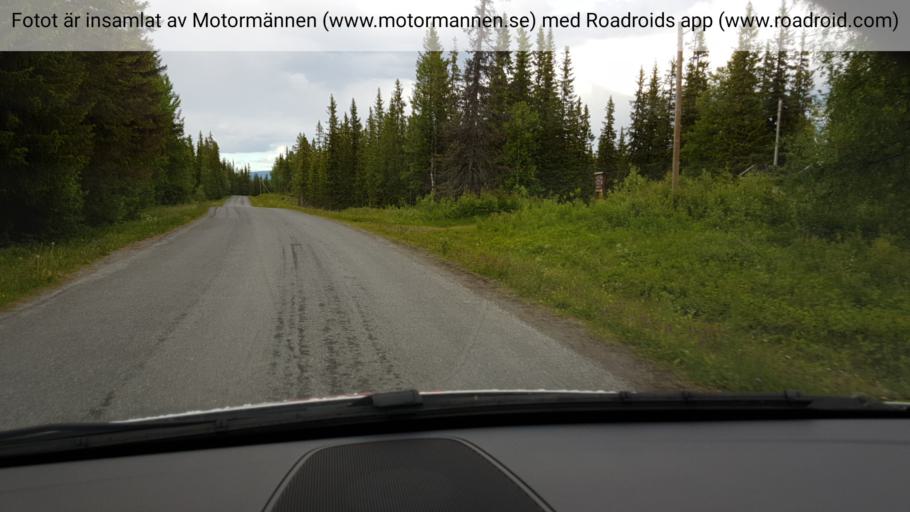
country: SE
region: Jaemtland
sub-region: Are Kommun
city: Are
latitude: 63.1596
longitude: 13.0725
